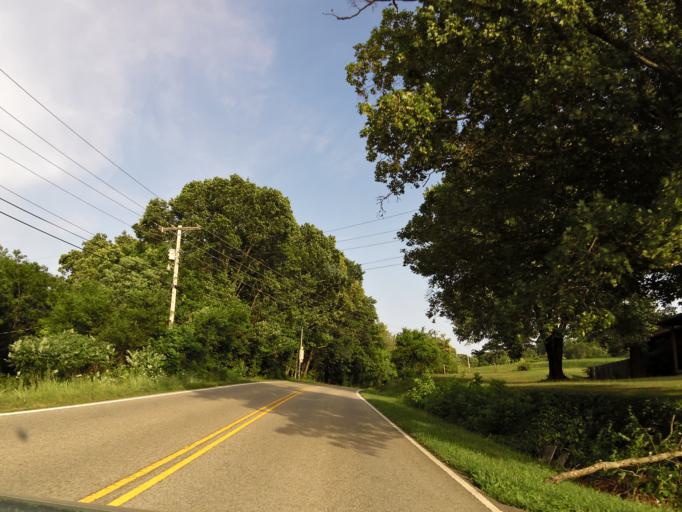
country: US
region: Tennessee
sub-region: Blount County
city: Eagleton Village
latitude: 35.8072
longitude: -83.9118
